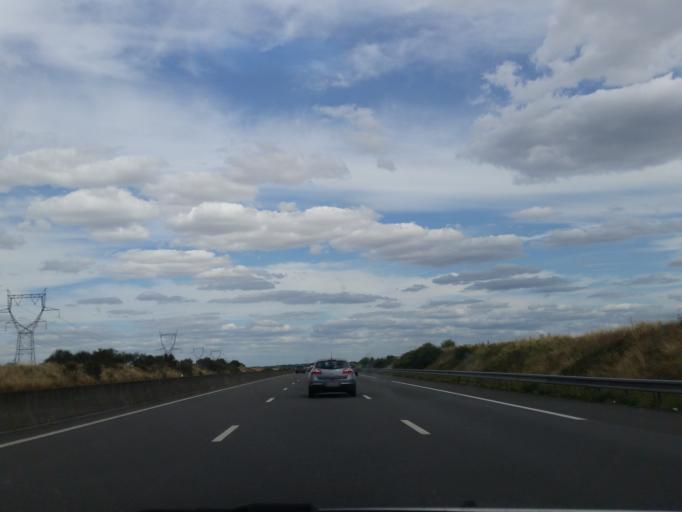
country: FR
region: Centre
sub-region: Departement du Loir-et-Cher
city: Herbault
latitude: 47.6161
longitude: 1.1662
